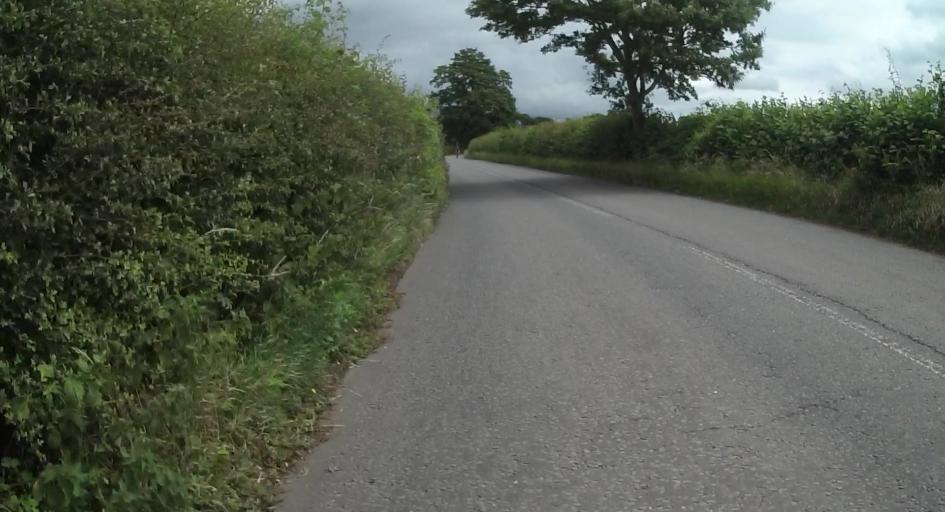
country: GB
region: England
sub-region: Surrey
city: Farnham
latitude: 51.2209
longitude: -0.8464
